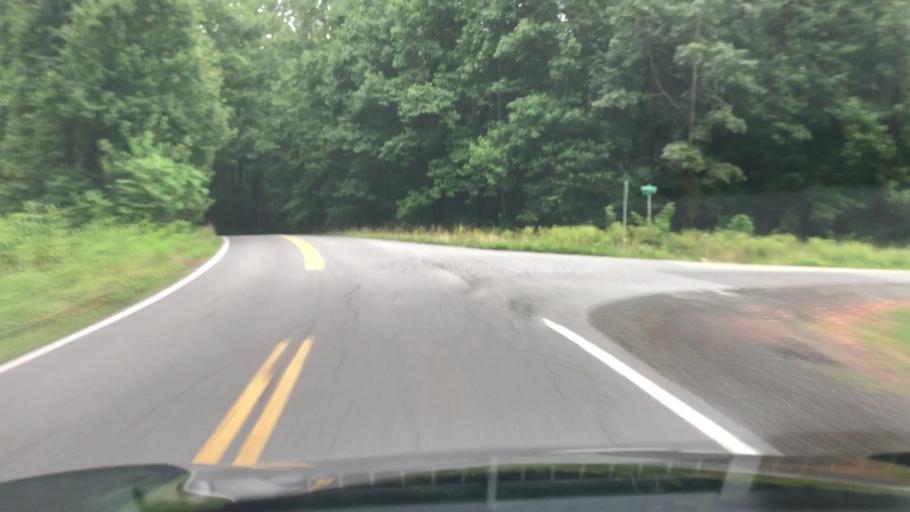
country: US
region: Virginia
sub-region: Fauquier County
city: Bealeton
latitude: 38.4970
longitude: -77.6017
